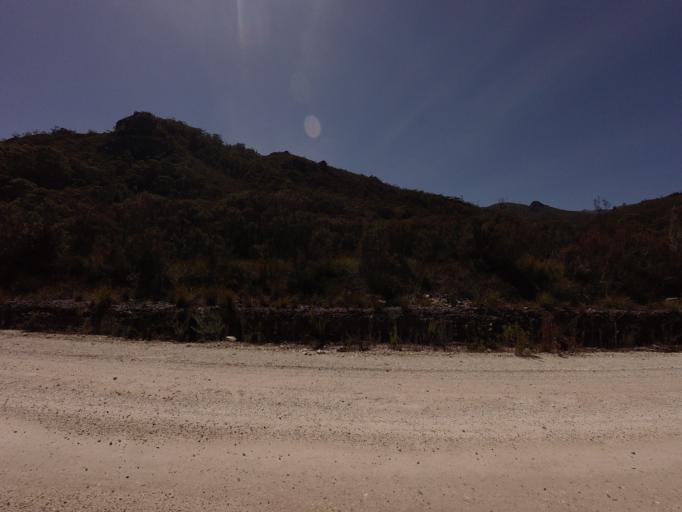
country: AU
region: Tasmania
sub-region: Huon Valley
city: Geeveston
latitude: -42.9455
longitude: 146.3508
